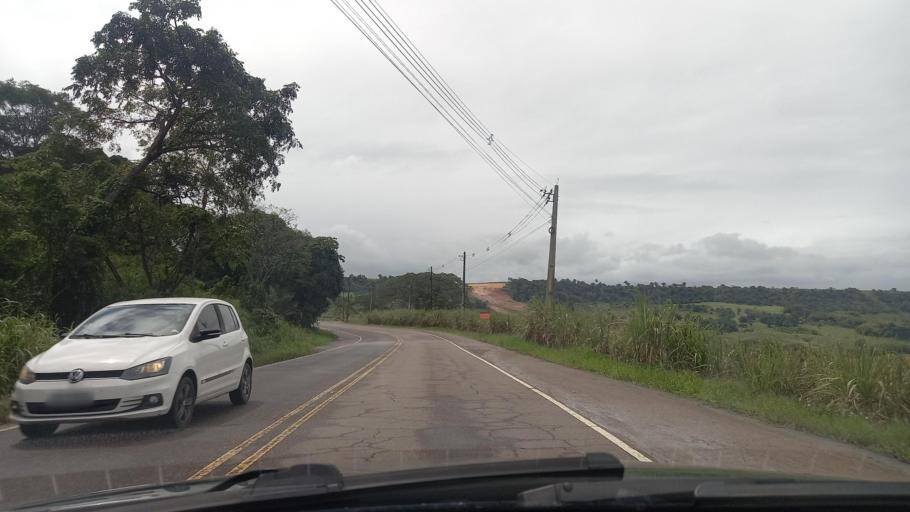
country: BR
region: Alagoas
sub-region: Sao Miguel Dos Campos
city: Sao Miguel dos Campos
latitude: -9.8207
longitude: -36.2207
